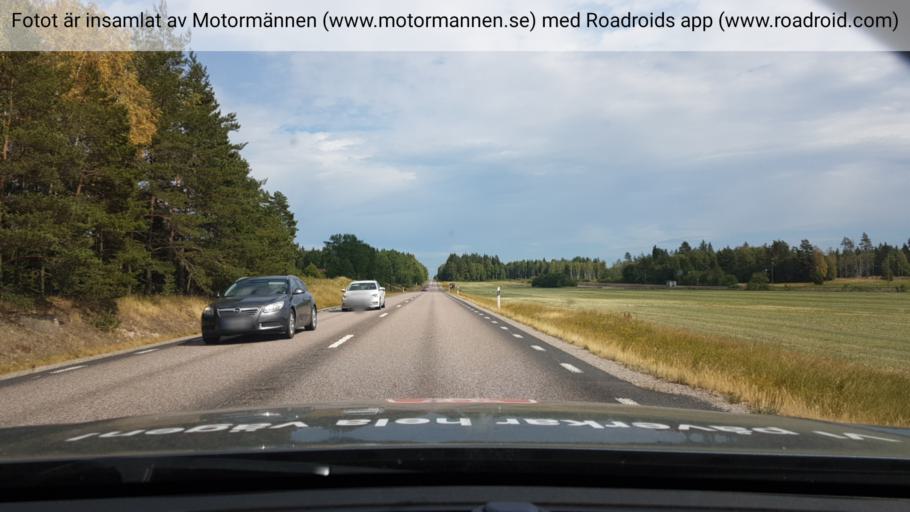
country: SE
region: Uppsala
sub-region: Enkopings Kommun
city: Orsundsbro
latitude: 59.8707
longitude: 17.3086
